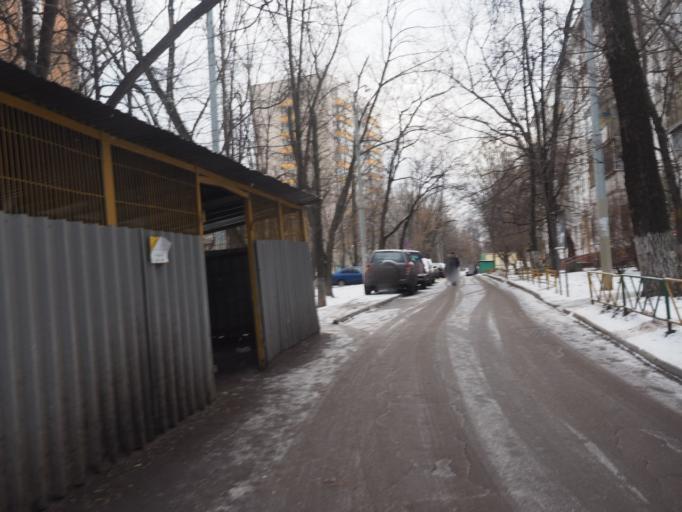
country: RU
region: Moscow
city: Orekhovo-Borisovo Severnoye
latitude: 55.6330
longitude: 37.6782
